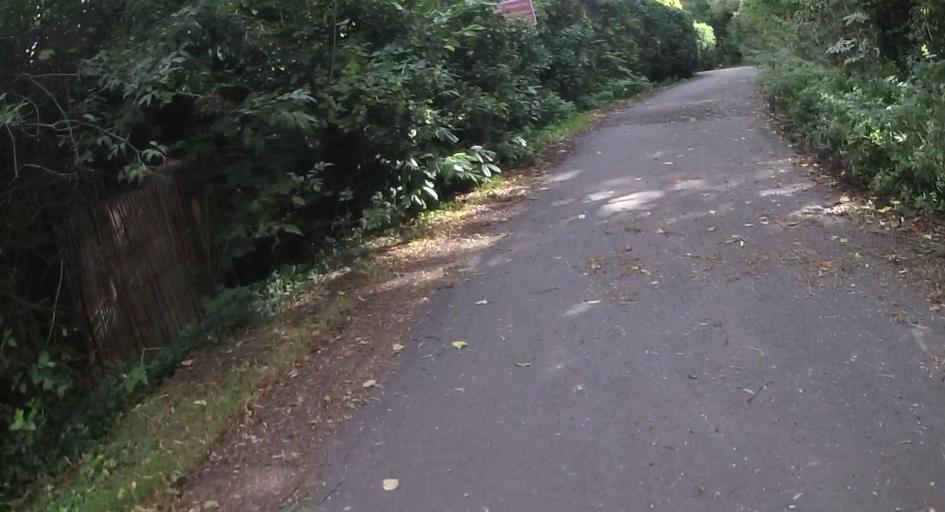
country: GB
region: England
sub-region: West Berkshire
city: Thatcham
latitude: 51.3906
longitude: -1.2393
